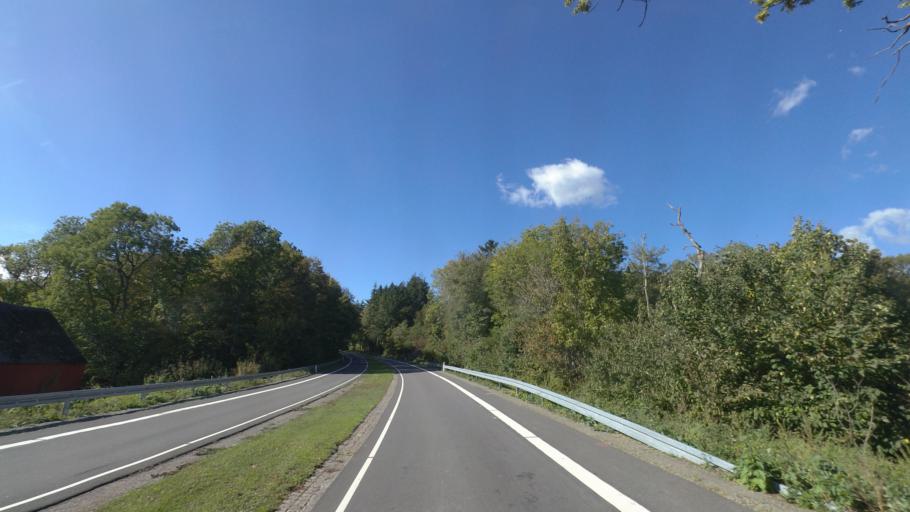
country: DK
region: Capital Region
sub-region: Bornholm Kommune
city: Akirkeby
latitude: 55.0646
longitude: 15.0201
